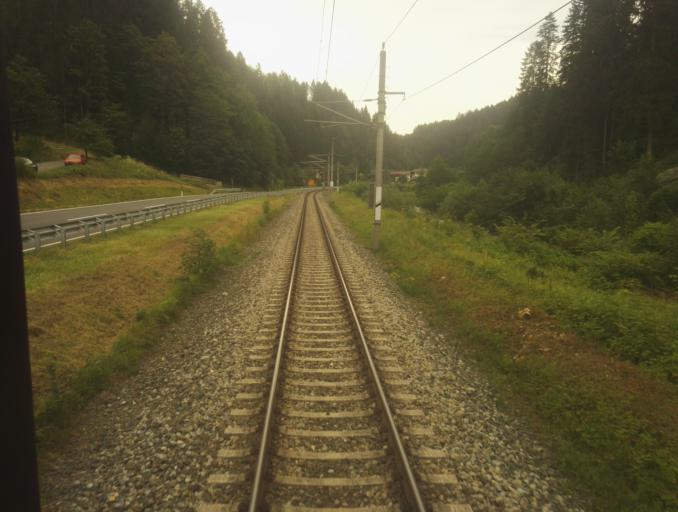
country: AT
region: Salzburg
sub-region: Politischer Bezirk Sankt Johann im Pongau
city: Bischofshofen
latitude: 47.4328
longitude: 13.2374
